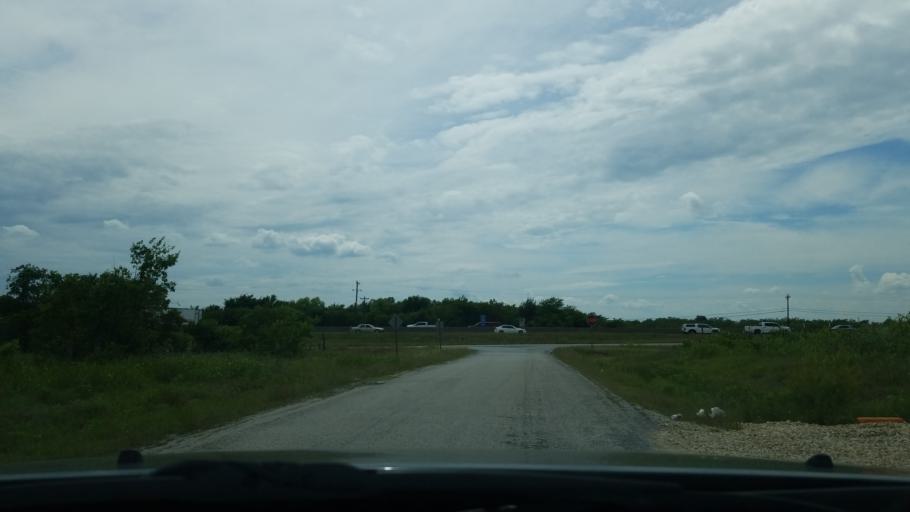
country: US
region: Texas
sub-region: Denton County
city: Sanger
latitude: 33.3033
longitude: -97.1764
